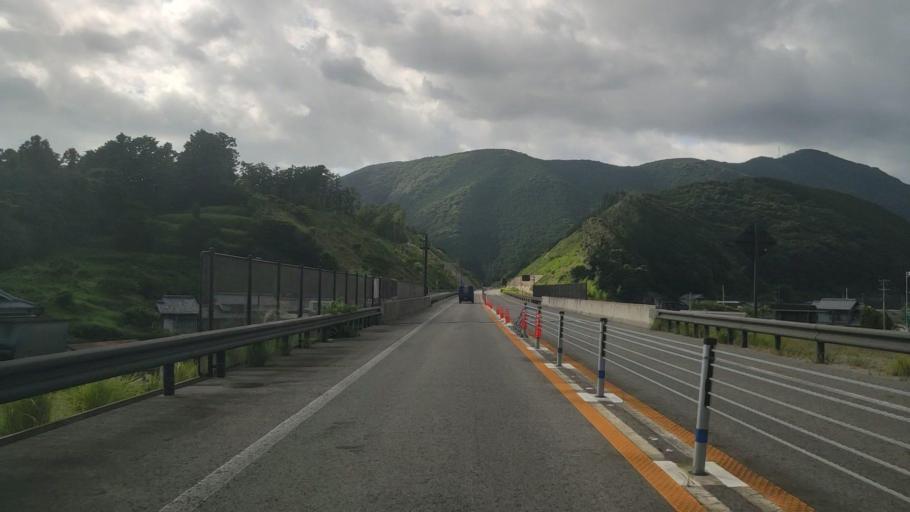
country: JP
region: Wakayama
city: Tanabe
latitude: 33.5556
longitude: 135.5097
